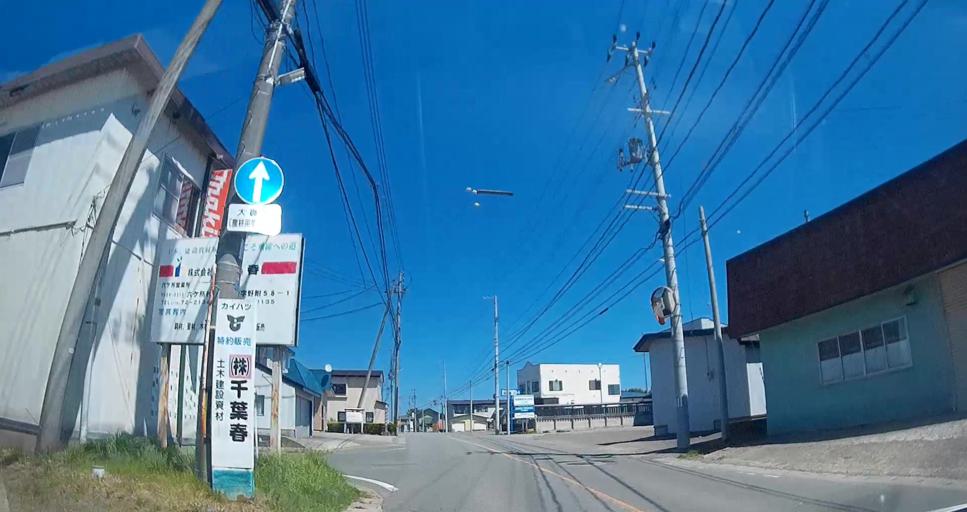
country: JP
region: Aomori
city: Misawa
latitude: 40.9633
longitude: 141.3744
